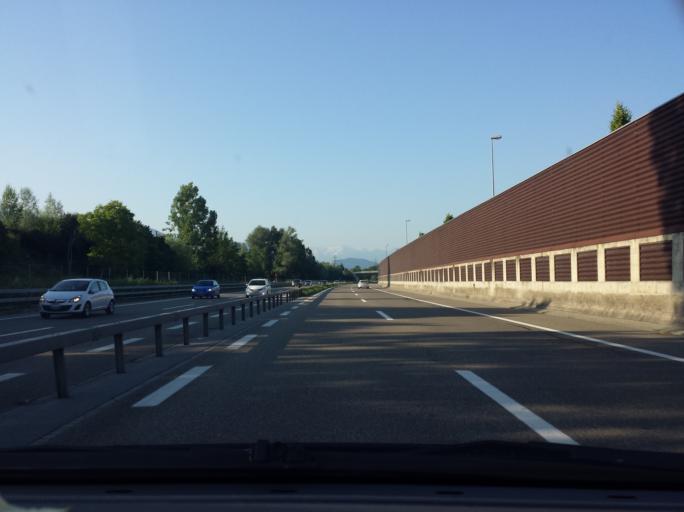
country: AT
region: Vorarlberg
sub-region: Politischer Bezirk Dornbirn
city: Lustenau
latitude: 47.4074
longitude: 9.6483
